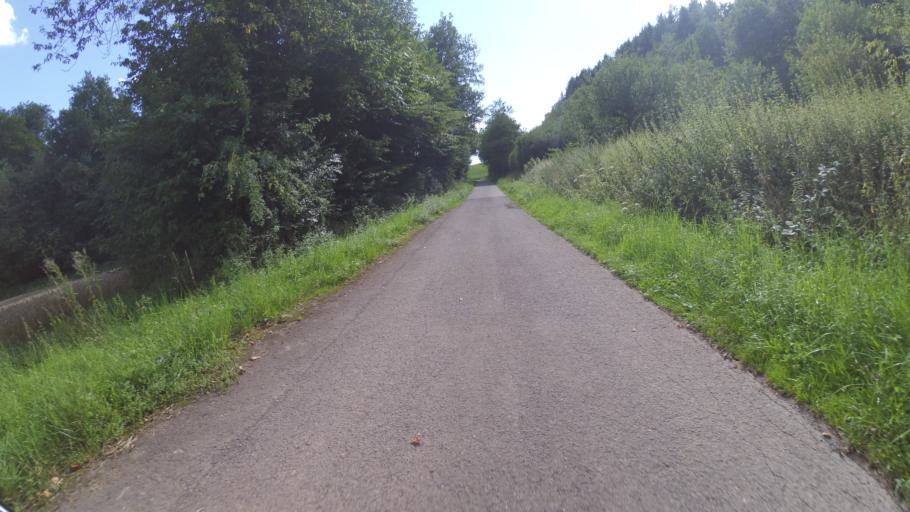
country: DE
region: Saarland
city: Marpingen
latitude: 49.4219
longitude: 7.0621
